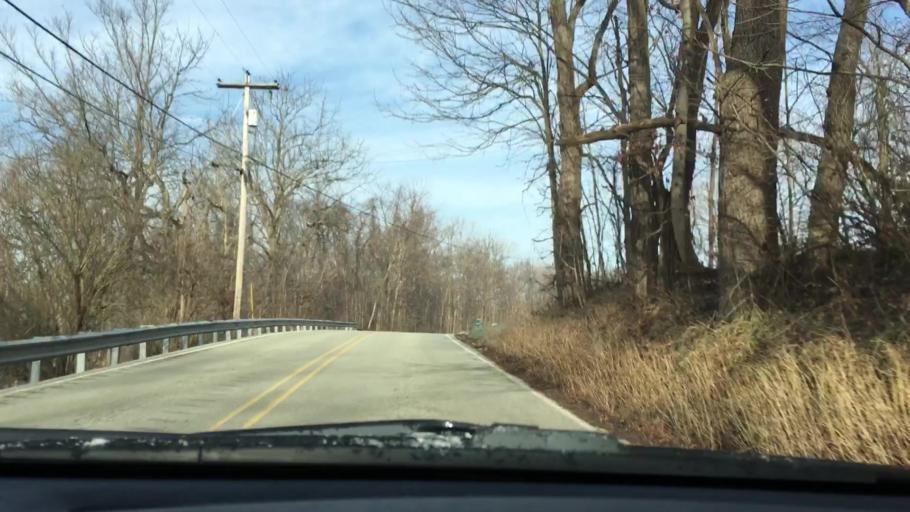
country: US
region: Pennsylvania
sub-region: Westmoreland County
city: Collinsburg
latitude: 40.2616
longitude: -79.7395
